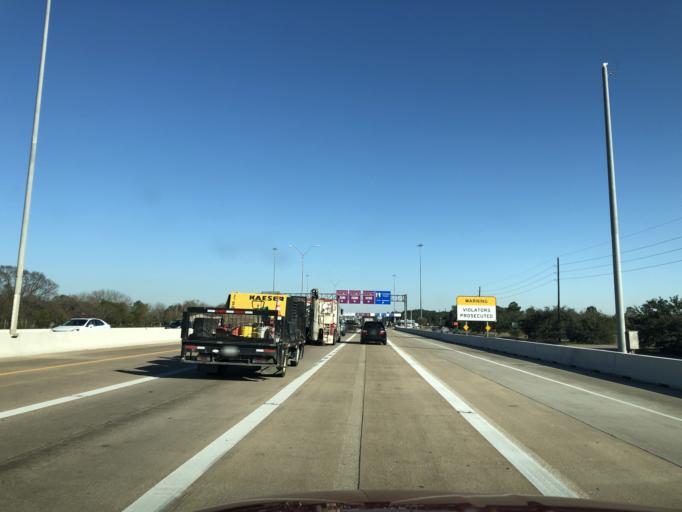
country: US
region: Texas
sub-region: Fort Bend County
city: Fresno
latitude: 29.5967
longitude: -95.4161
